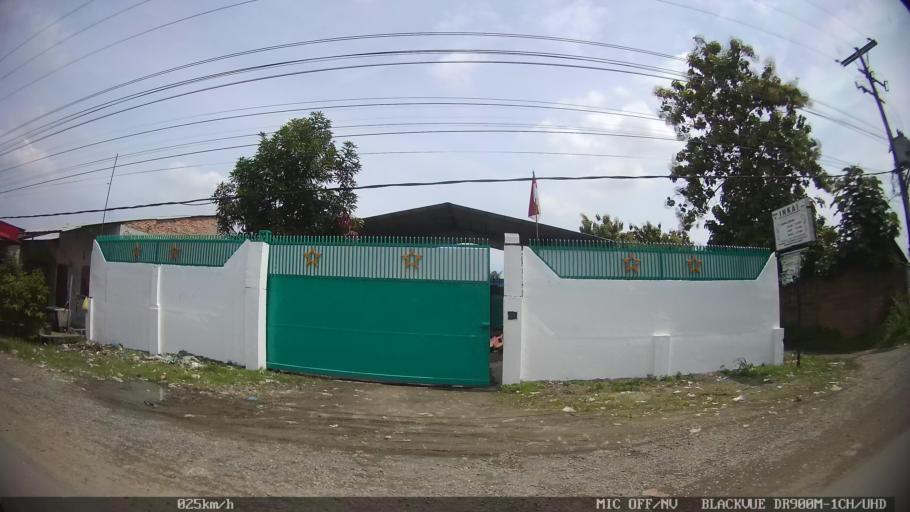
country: ID
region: North Sumatra
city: Medan
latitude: 3.6507
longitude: 98.7088
